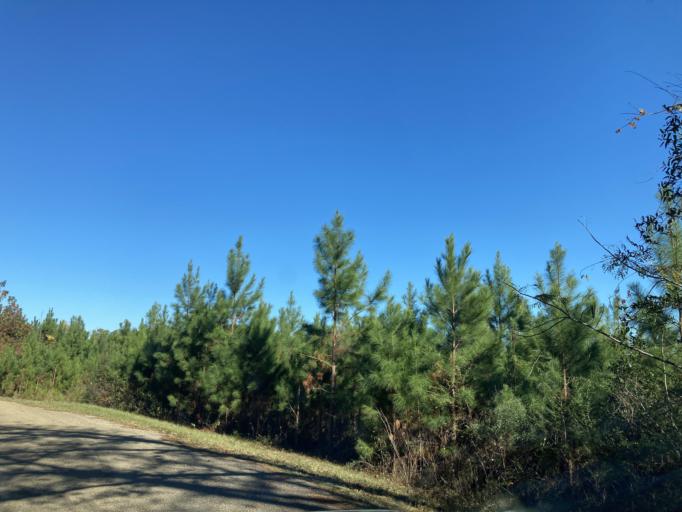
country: US
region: Mississippi
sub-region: Lamar County
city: Sumrall
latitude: 31.3062
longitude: -89.6066
